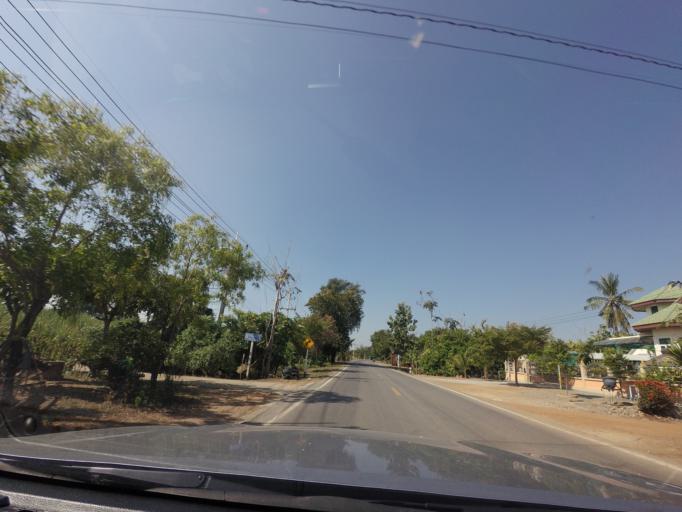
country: TH
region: Sukhothai
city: Sawankhalok
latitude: 17.3482
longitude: 99.8234
